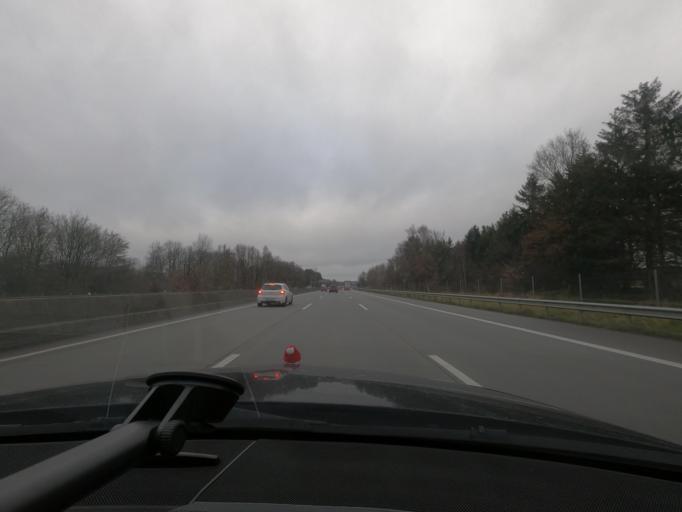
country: DE
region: Schleswig-Holstein
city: Quickborn
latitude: 53.7085
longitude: 9.9405
